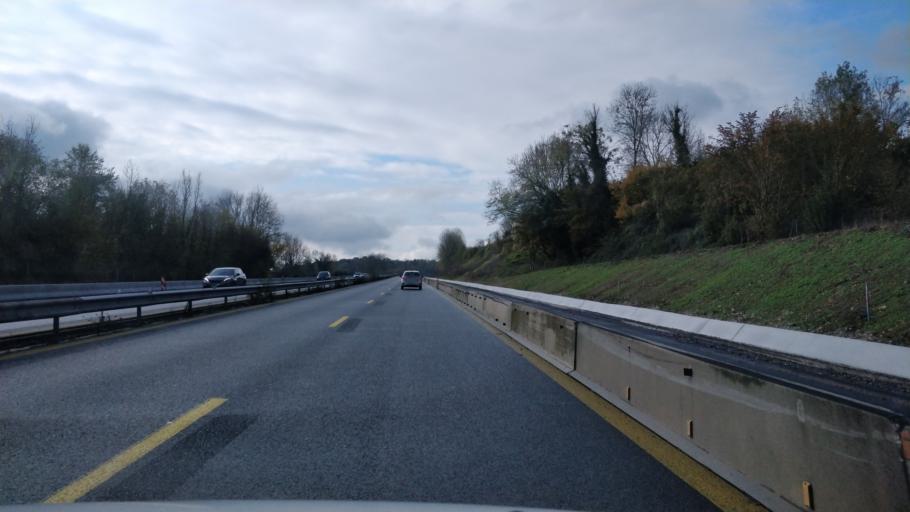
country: FR
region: Lower Normandy
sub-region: Departement du Calvados
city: Saint-Gatien-des-Bois
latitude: 49.2678
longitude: 0.1698
